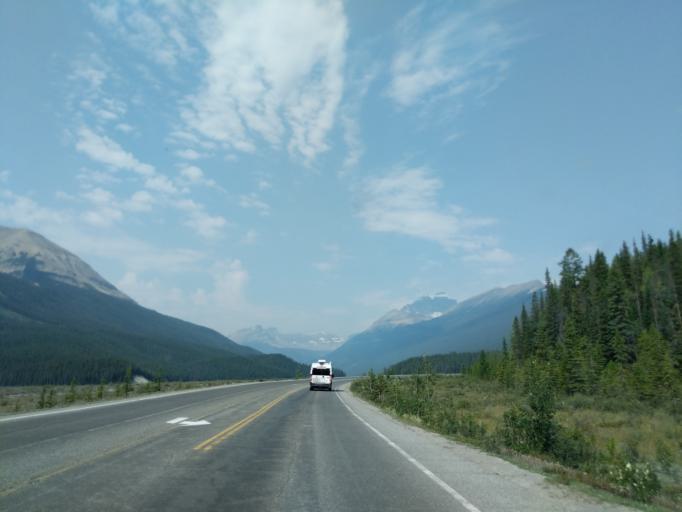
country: CA
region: British Columbia
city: Golden
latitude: 52.0684
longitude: -116.9101
